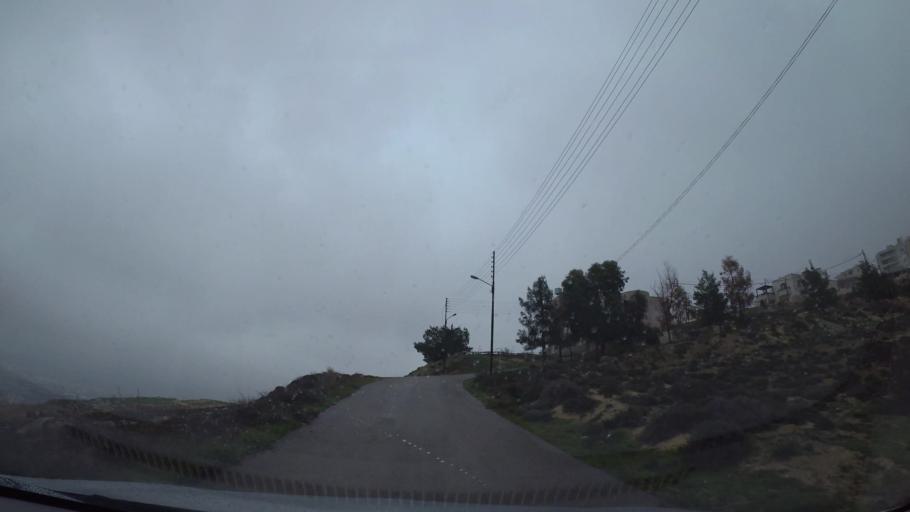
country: JO
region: Amman
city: Al Jubayhah
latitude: 32.0373
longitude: 35.8506
